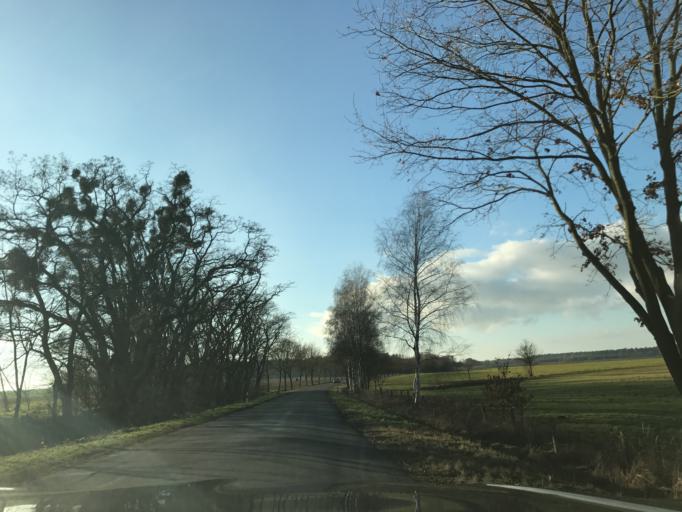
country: DE
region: Saxony-Anhalt
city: Loburg
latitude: 52.1721
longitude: 12.0379
